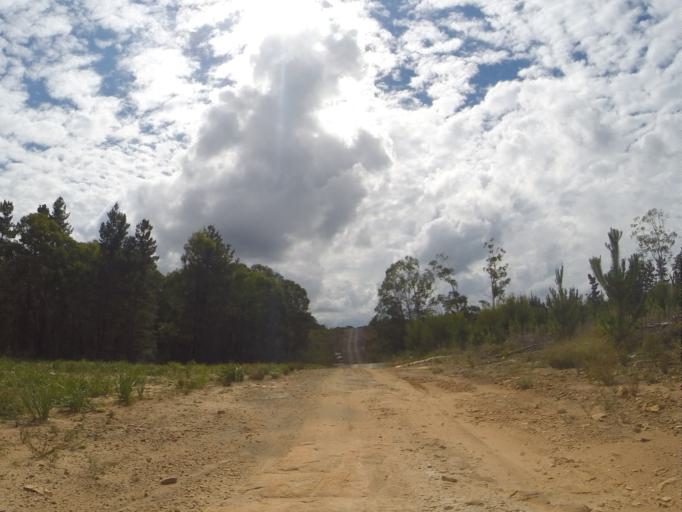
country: AU
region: New South Wales
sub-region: Wingecarribee
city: Moss Vale
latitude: -34.5249
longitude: 150.2246
